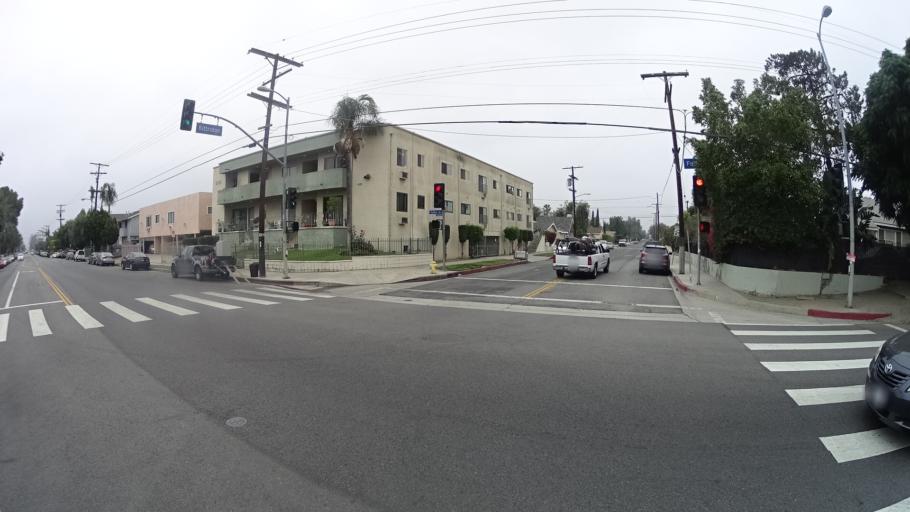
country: US
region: California
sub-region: Los Angeles County
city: Van Nuys
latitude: 34.1904
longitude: -118.4225
